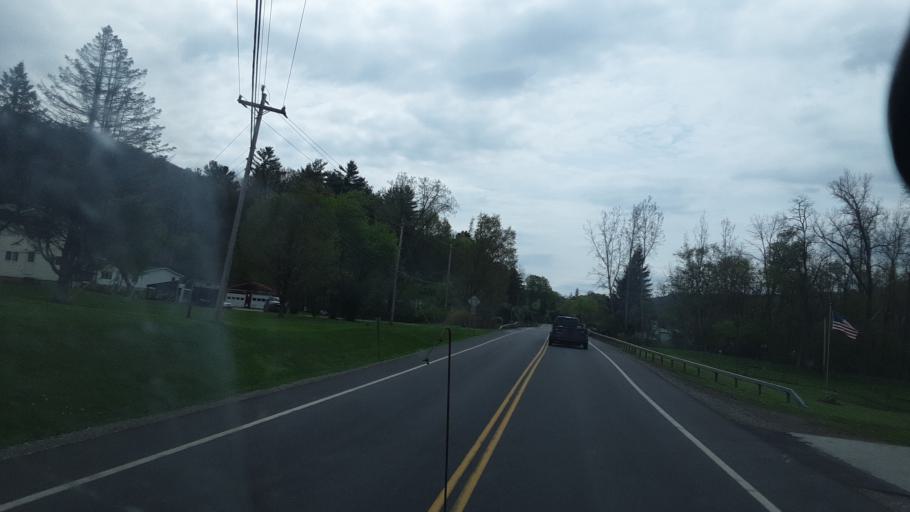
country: US
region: New York
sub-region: Steuben County
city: Canisteo
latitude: 42.2308
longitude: -77.5765
